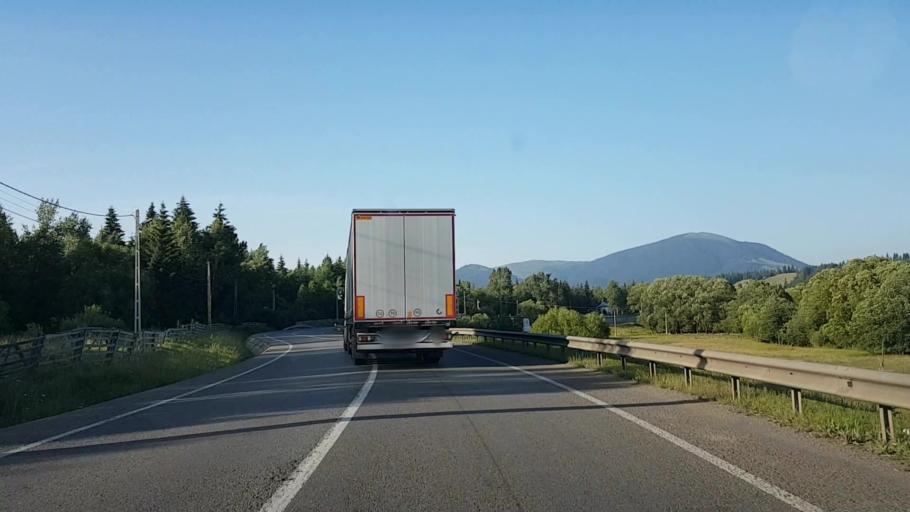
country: RO
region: Suceava
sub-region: Comuna Poiana Stampei
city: Poiana Stampei
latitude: 47.3353
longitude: 25.1635
